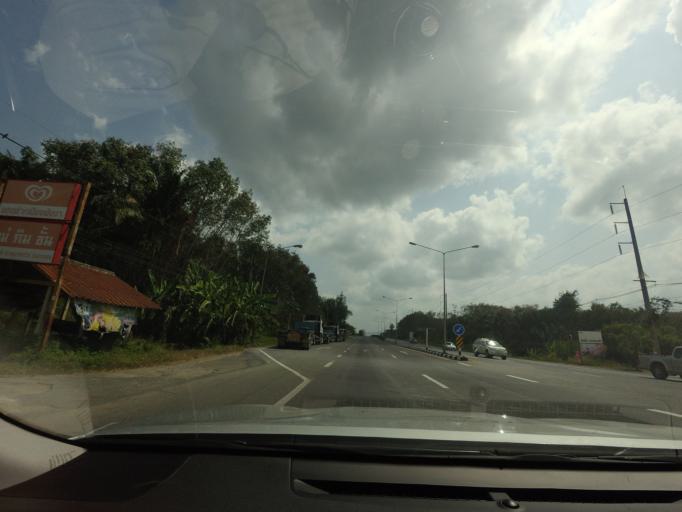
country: TH
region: Phangnga
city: Thap Put
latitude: 8.5091
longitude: 98.6544
